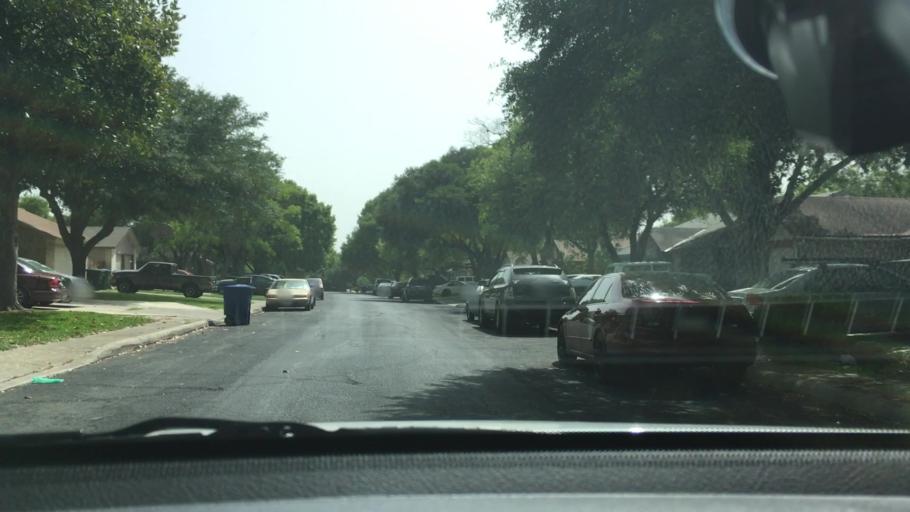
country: US
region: Texas
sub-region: Bexar County
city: Live Oak
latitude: 29.5937
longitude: -98.3784
